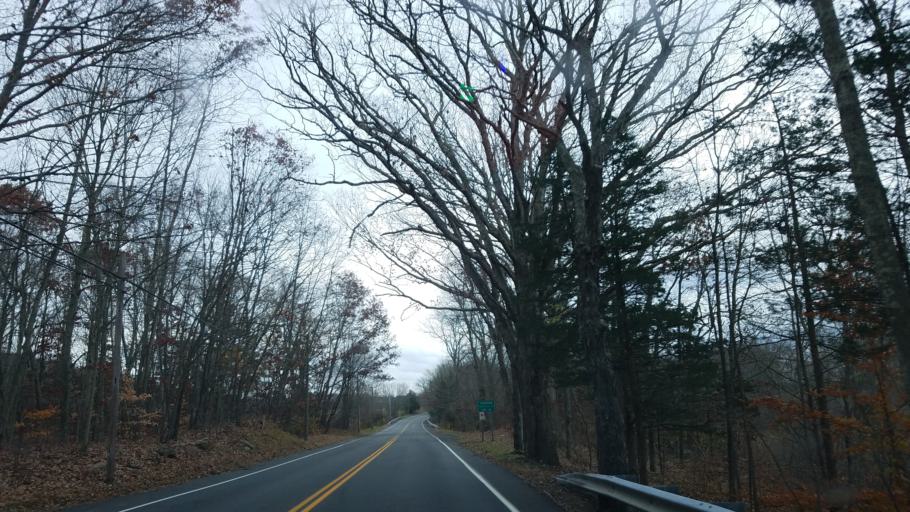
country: US
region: Connecticut
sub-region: New London County
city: Colchester
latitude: 41.5747
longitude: -72.2633
